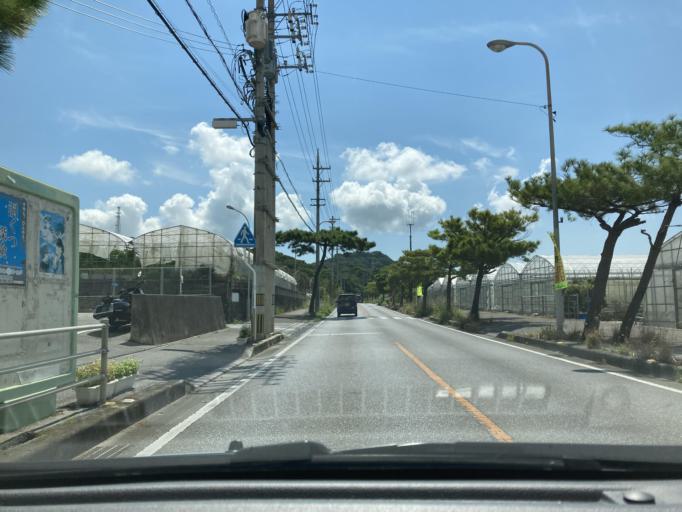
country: JP
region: Okinawa
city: Tomigusuku
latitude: 26.1747
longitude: 127.7512
